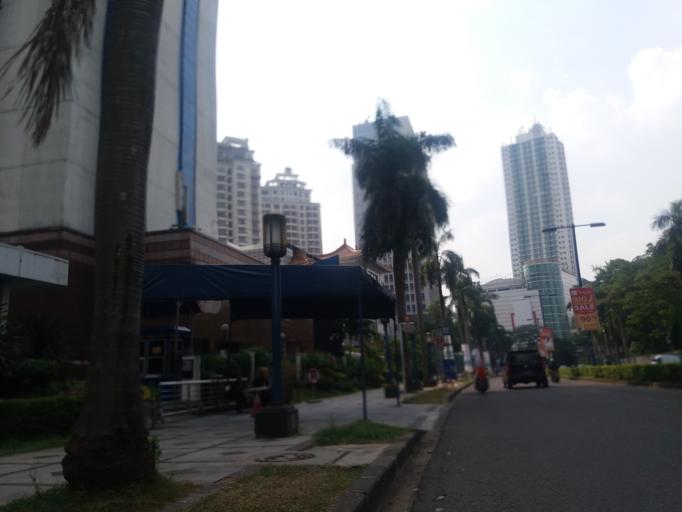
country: ID
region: Jakarta Raya
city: Jakarta
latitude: -6.2267
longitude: 106.8258
